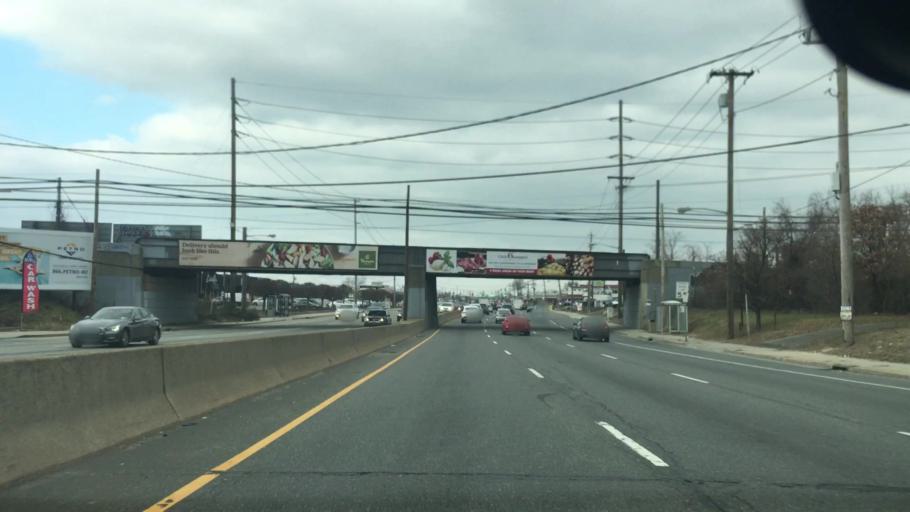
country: US
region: New York
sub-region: Suffolk County
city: East Farmingdale
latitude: 40.7394
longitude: -73.4231
